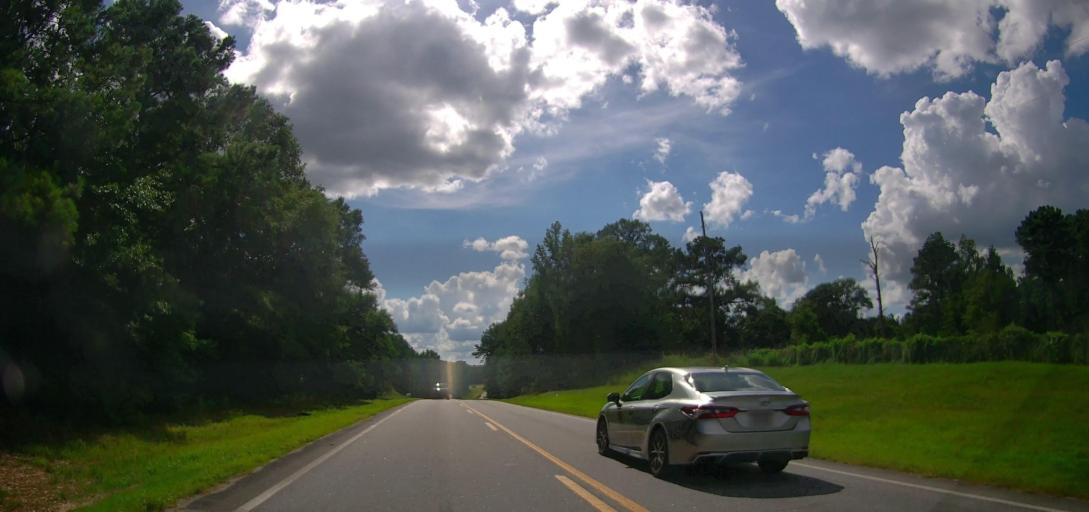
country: US
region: Alabama
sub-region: Lee County
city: Opelika
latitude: 32.4398
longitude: -85.3096
